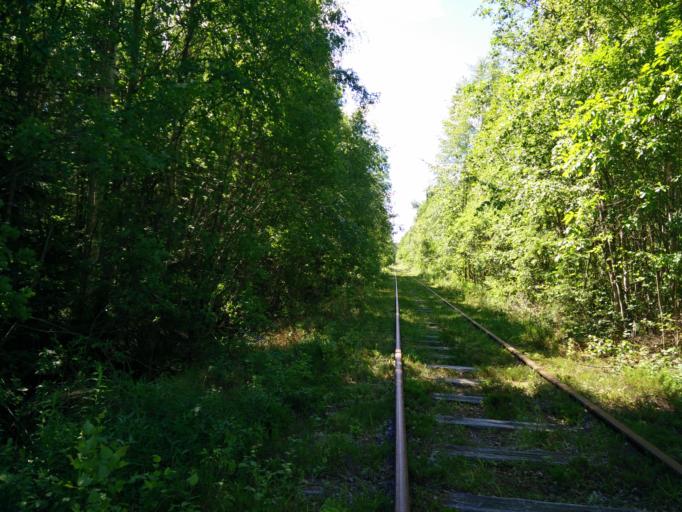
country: SE
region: Gaevleborg
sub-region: Hudiksvalls Kommun
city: Delsbo
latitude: 61.7956
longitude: 16.5323
